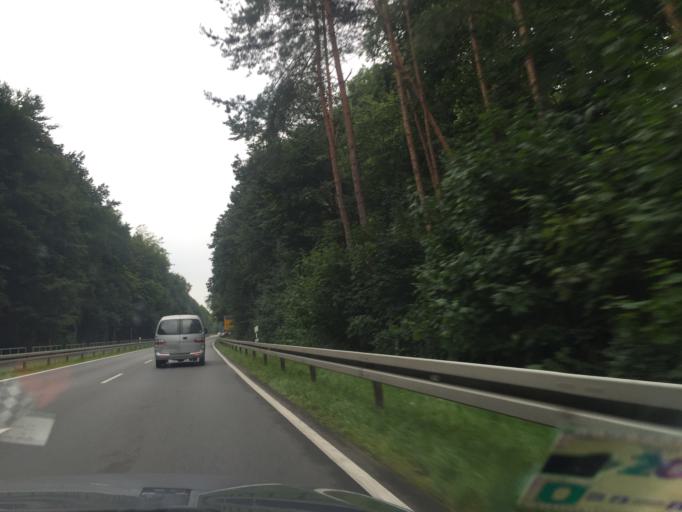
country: DE
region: Brandenburg
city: Wandlitz
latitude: 52.7351
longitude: 13.4928
